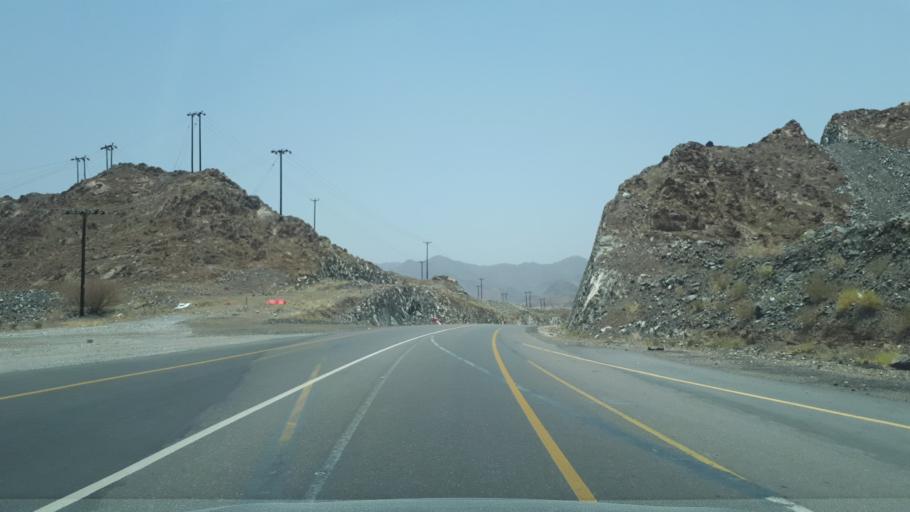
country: OM
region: Al Batinah
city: Rustaq
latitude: 23.4156
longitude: 57.3023
